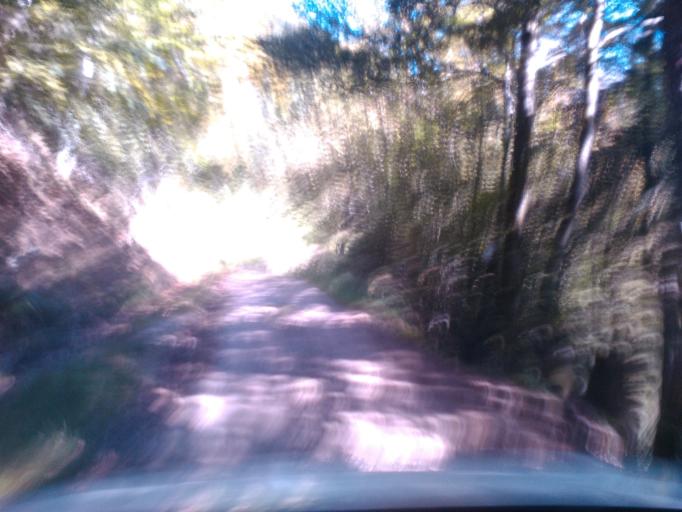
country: FR
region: Lorraine
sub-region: Departement des Vosges
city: Senones
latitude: 48.4204
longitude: 6.9841
